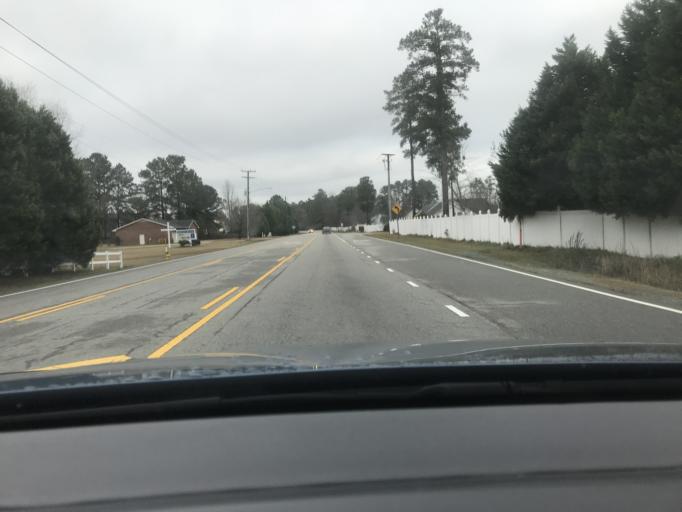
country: US
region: North Carolina
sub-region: Hoke County
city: Rockfish
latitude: 35.0421
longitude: -79.0078
